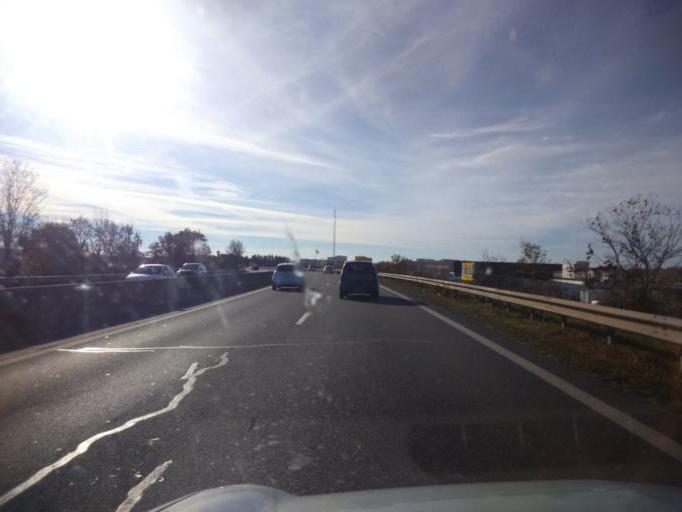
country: FR
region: Poitou-Charentes
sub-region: Departement de la Charente-Maritime
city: Perigny
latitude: 46.1616
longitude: -1.1219
